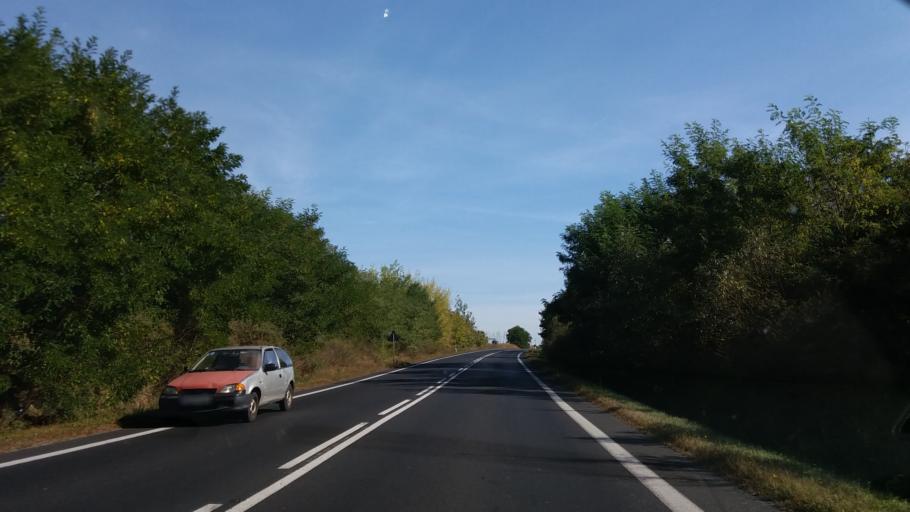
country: PL
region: Greater Poland Voivodeship
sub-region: Powiat miedzychodzki
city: Kwilcz
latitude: 52.5525
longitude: 16.0997
